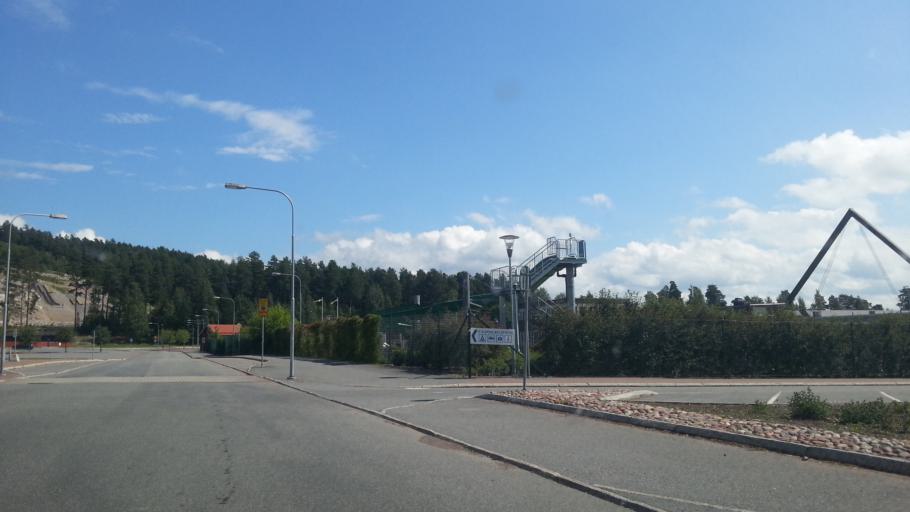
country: SE
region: Dalarna
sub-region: Faluns Kommun
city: Falun
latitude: 60.6190
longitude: 15.6543
